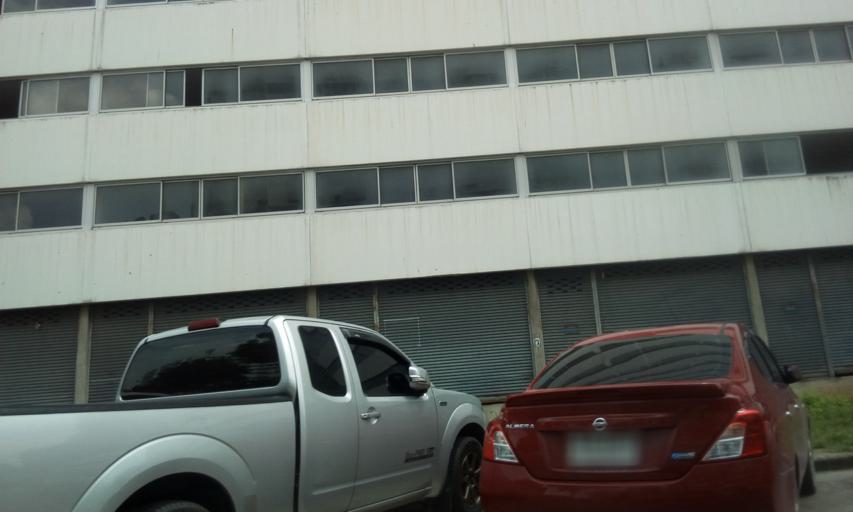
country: TH
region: Bangkok
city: Lak Si
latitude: 13.9114
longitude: 100.5547
